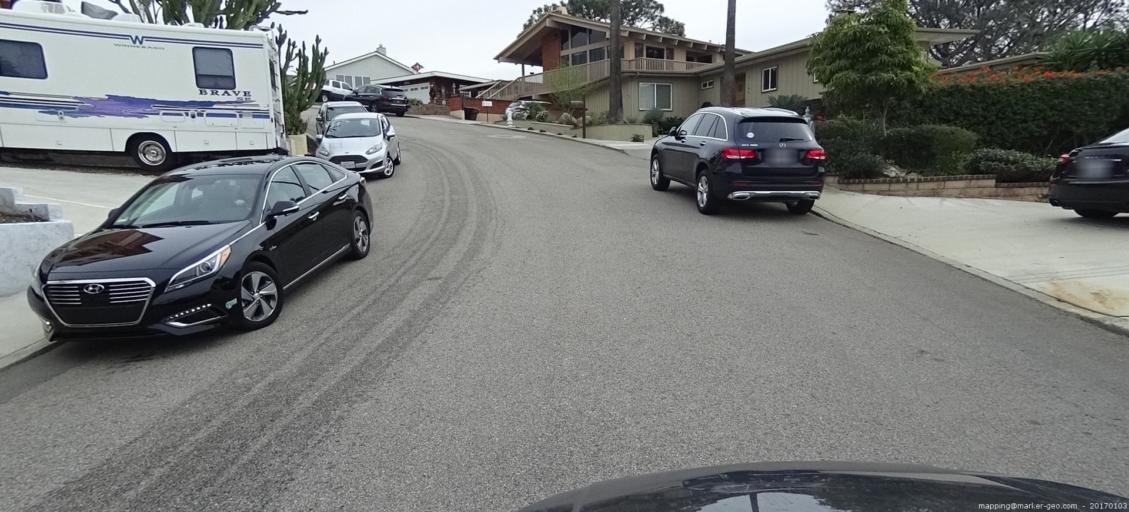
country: US
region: California
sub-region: Orange County
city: San Juan Capistrano
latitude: 33.4629
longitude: -117.6560
